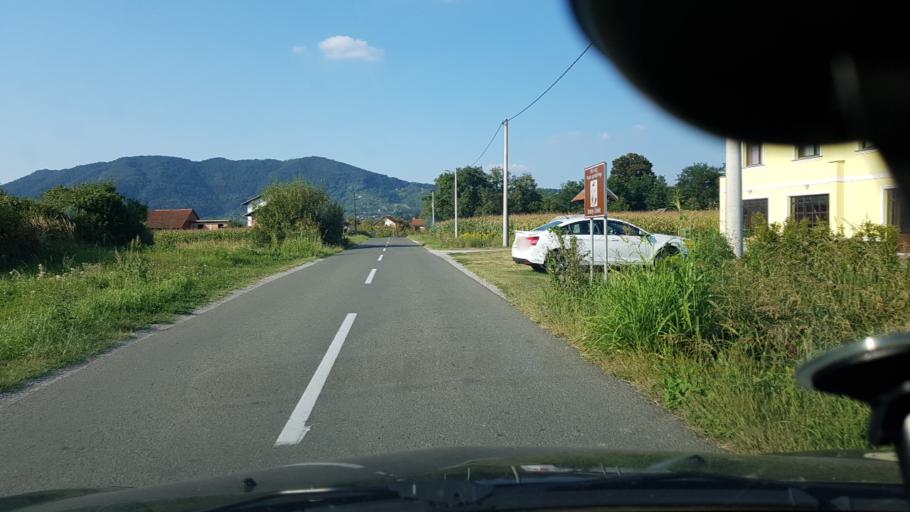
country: SI
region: Bistrica ob Sotli
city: Bistrica ob Sotli
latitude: 46.0276
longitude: 15.7314
